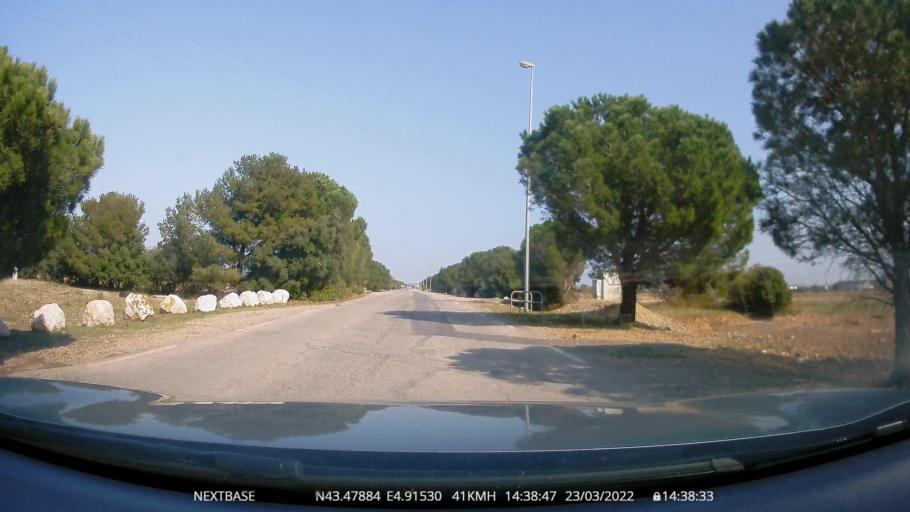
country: FR
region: Provence-Alpes-Cote d'Azur
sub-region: Departement des Bouches-du-Rhone
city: Fos-sur-Mer
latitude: 43.4790
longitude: 4.9153
